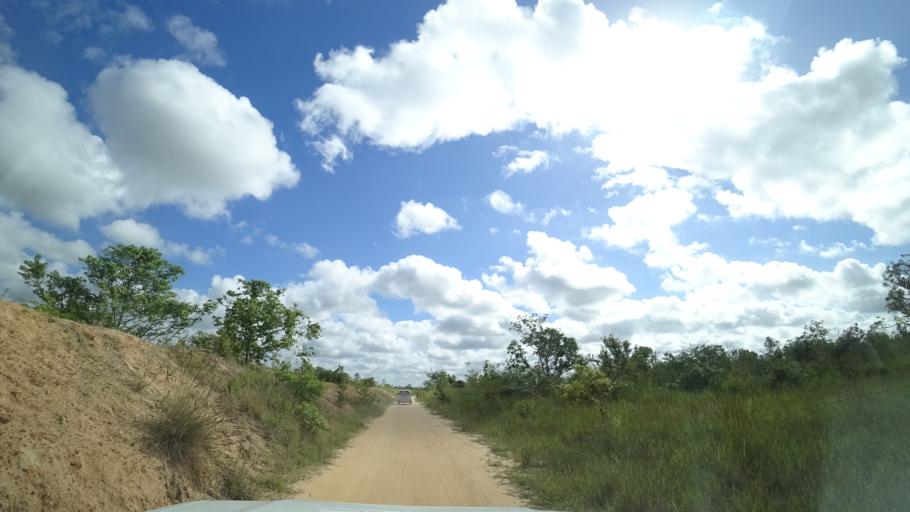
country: MZ
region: Sofala
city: Beira
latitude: -19.6197
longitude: 35.0605
